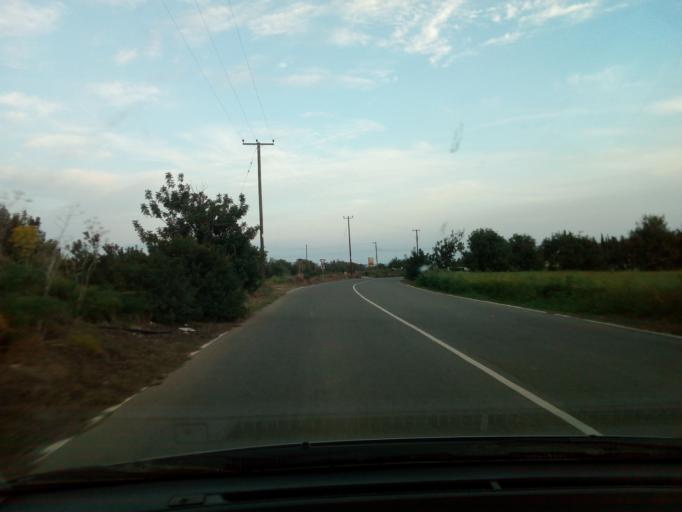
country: CY
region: Larnaka
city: Tersefanou
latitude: 34.8023
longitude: 33.5057
